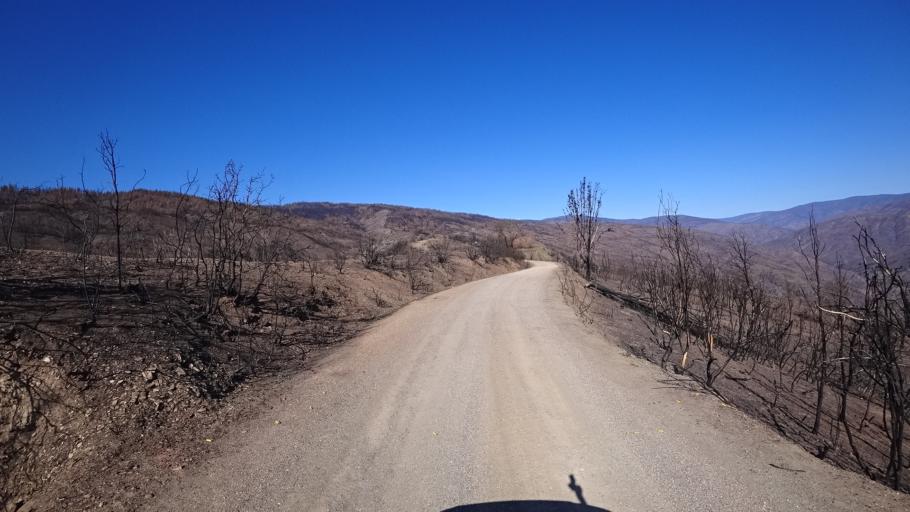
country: US
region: California
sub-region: Tehama County
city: Rancho Tehama Reserve
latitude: 39.6666
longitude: -122.6658
